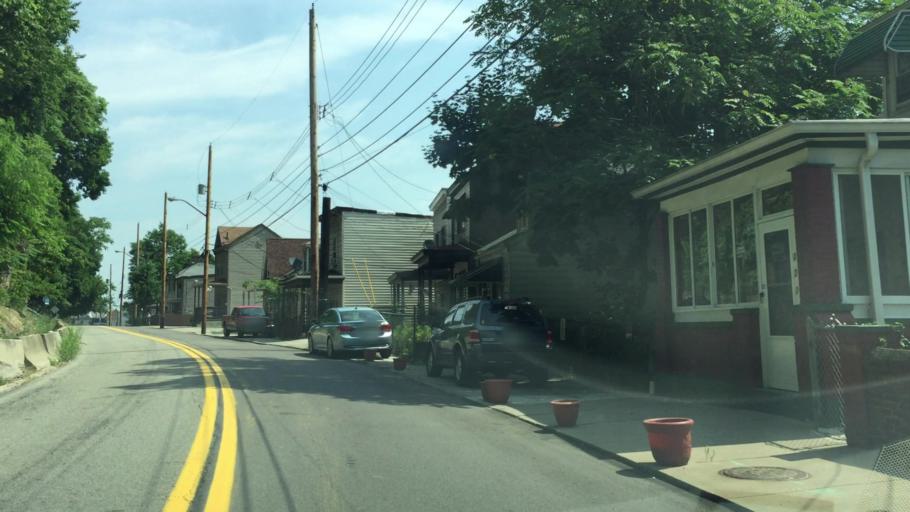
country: US
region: Pennsylvania
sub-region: Allegheny County
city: Mount Oliver
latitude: 40.4190
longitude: -79.9647
